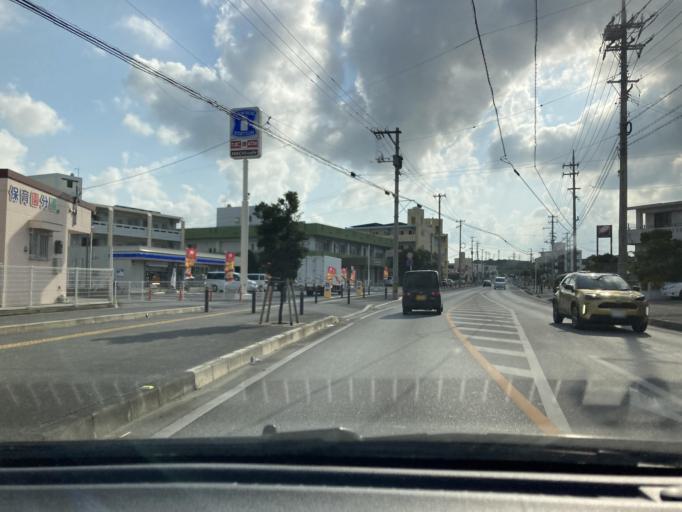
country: JP
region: Okinawa
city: Tomigusuku
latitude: 26.1513
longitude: 127.7172
